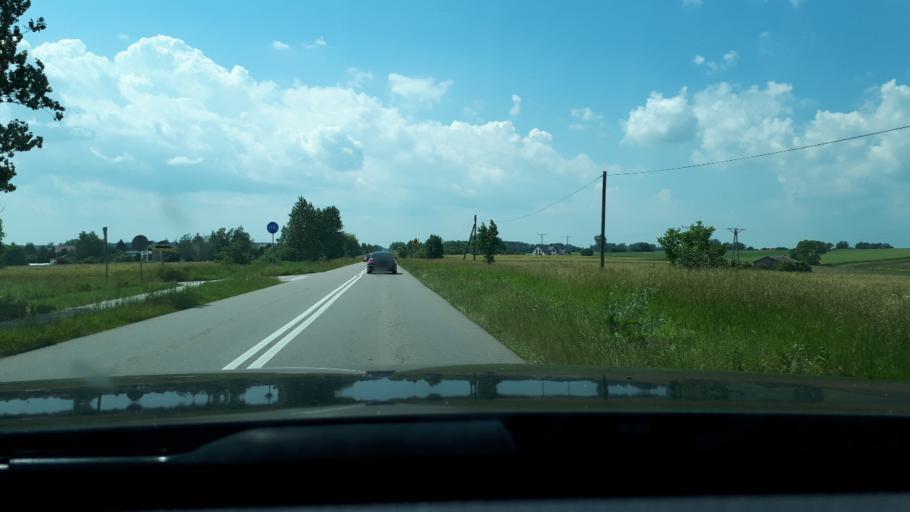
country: PL
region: Podlasie
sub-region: Powiat bialostocki
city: Choroszcz
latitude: 53.1301
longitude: 23.0275
